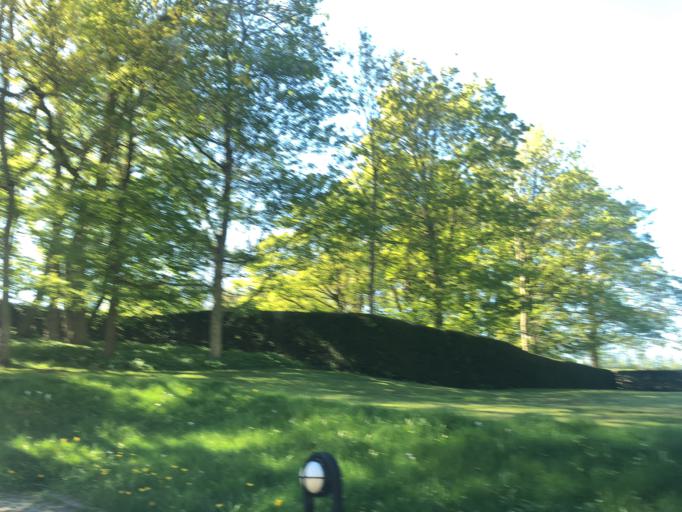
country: DK
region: Zealand
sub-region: Koge Kommune
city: Koge
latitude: 55.4176
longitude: 12.1495
